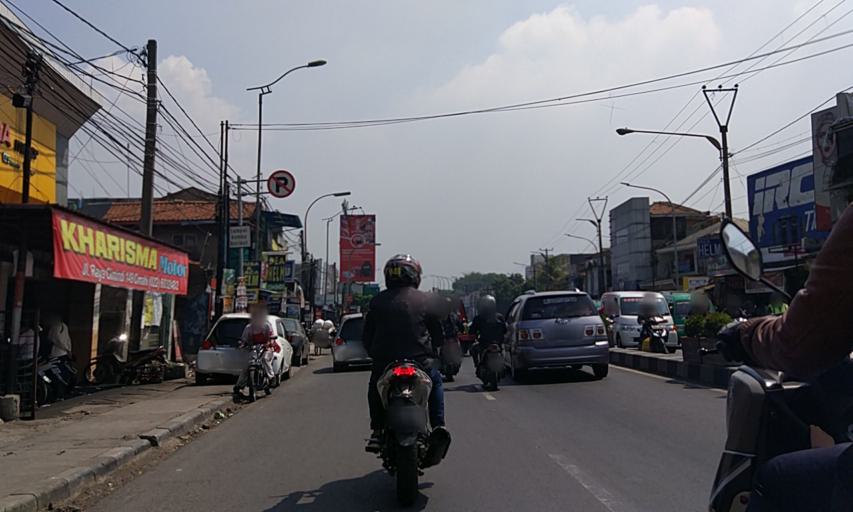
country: ID
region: West Java
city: Cimahi
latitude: -6.8996
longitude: 107.5624
